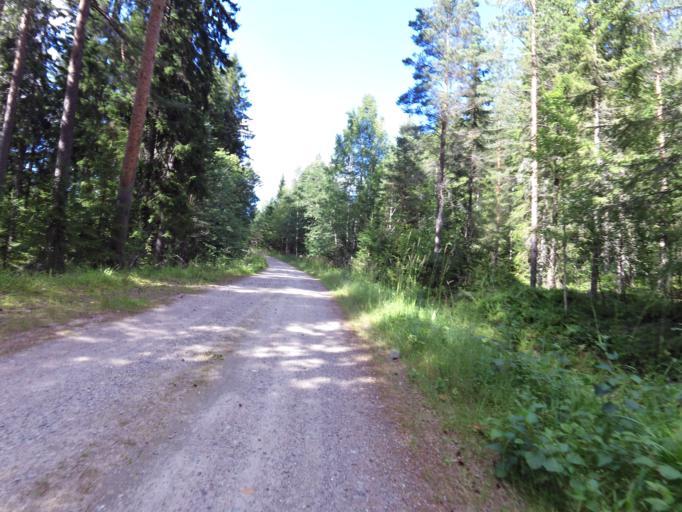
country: SE
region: Dalarna
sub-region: Faluns Kommun
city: Svardsjo
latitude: 60.6690
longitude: 15.9111
